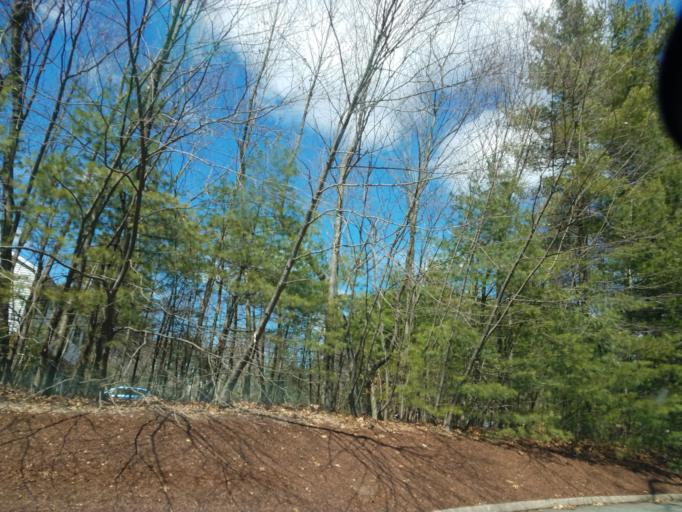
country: US
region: Connecticut
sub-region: Hartford County
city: Canton Valley
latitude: 41.8127
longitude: -72.8604
